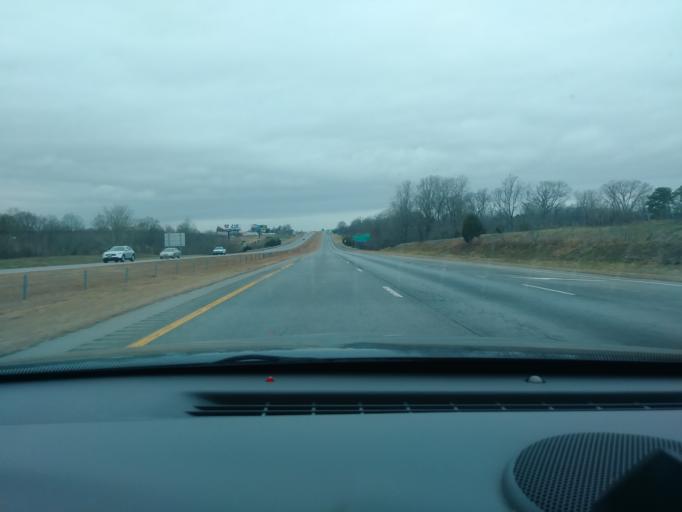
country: US
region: North Carolina
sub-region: Yadkin County
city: Yadkinville
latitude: 36.1172
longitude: -80.7786
